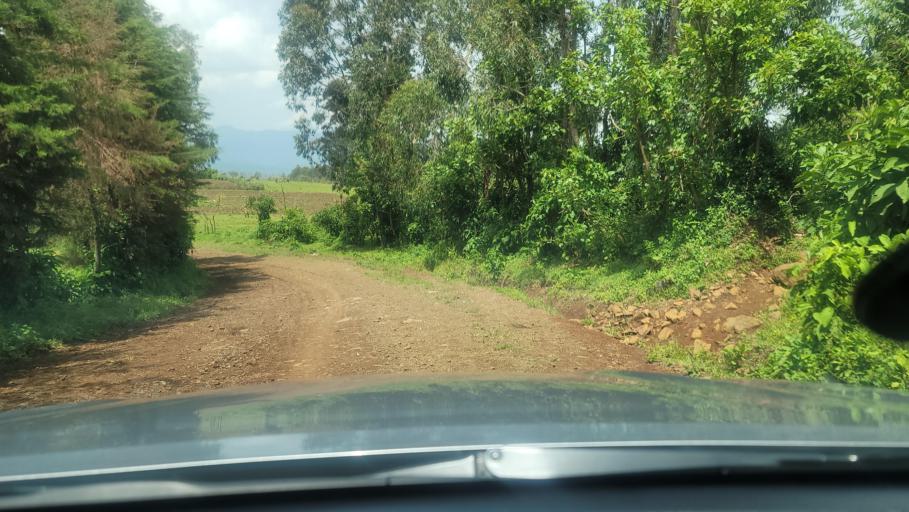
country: ET
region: Oromiya
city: Agaro
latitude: 7.8346
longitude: 36.4052
